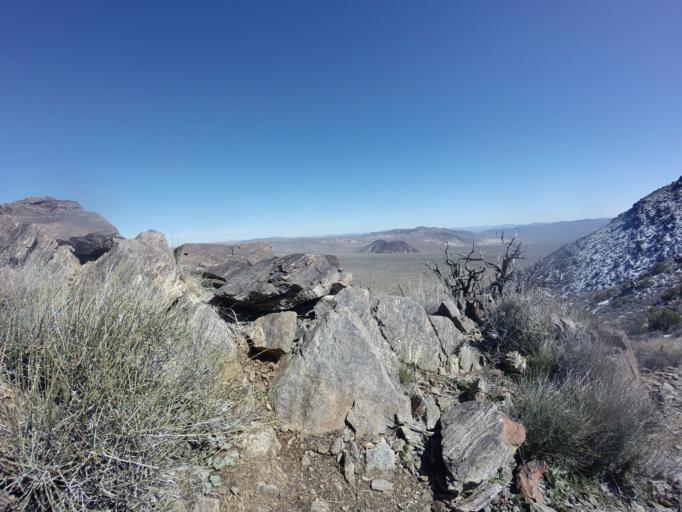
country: US
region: California
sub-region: San Bernardino County
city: Twentynine Palms
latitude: 33.9331
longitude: -116.1302
